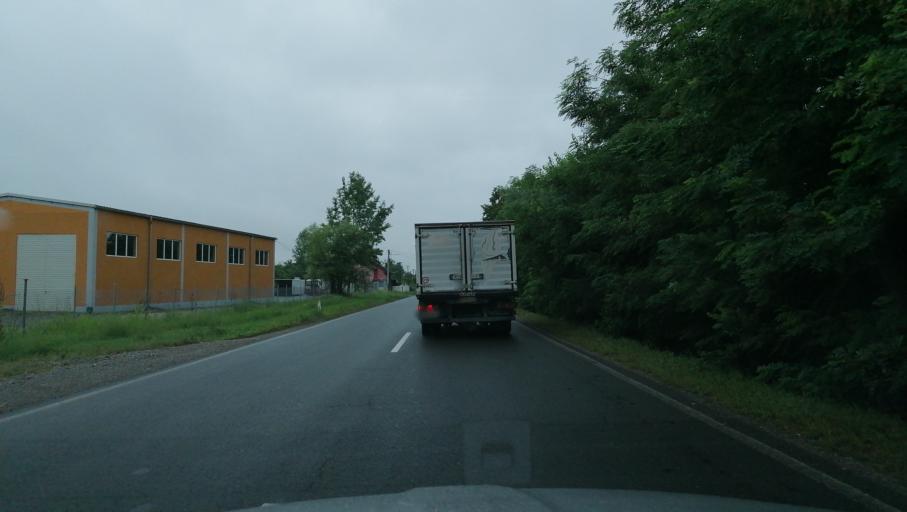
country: RS
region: Central Serbia
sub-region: Rasinski Okrug
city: Krusevac
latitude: 43.5867
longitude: 21.2542
